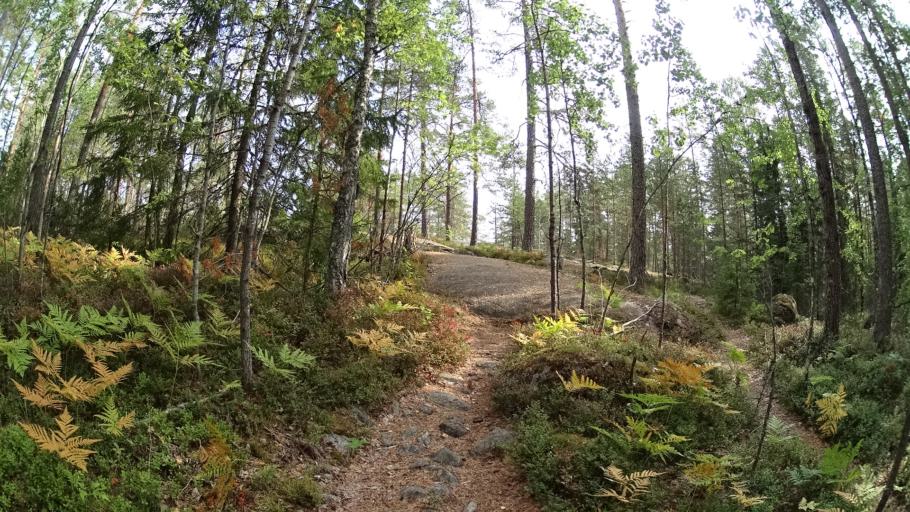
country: FI
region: Uusimaa
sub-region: Helsinki
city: Espoo
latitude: 60.2970
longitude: 24.5813
